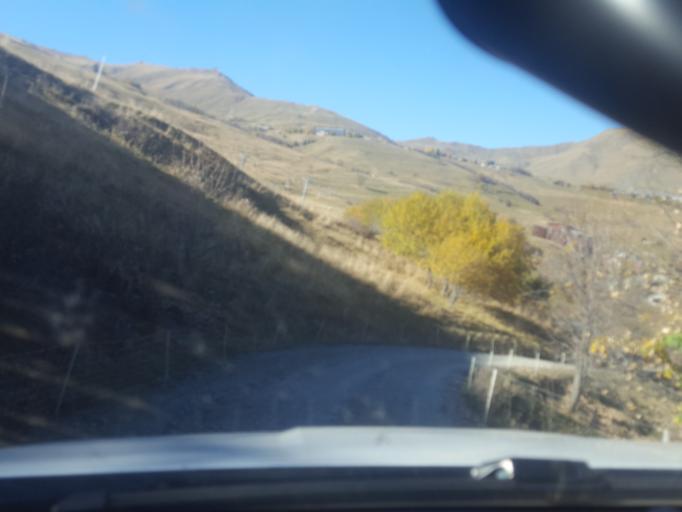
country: FR
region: Rhone-Alpes
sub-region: Departement de la Savoie
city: Saint-Jean-de-Maurienne
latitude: 45.2376
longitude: 6.2679
